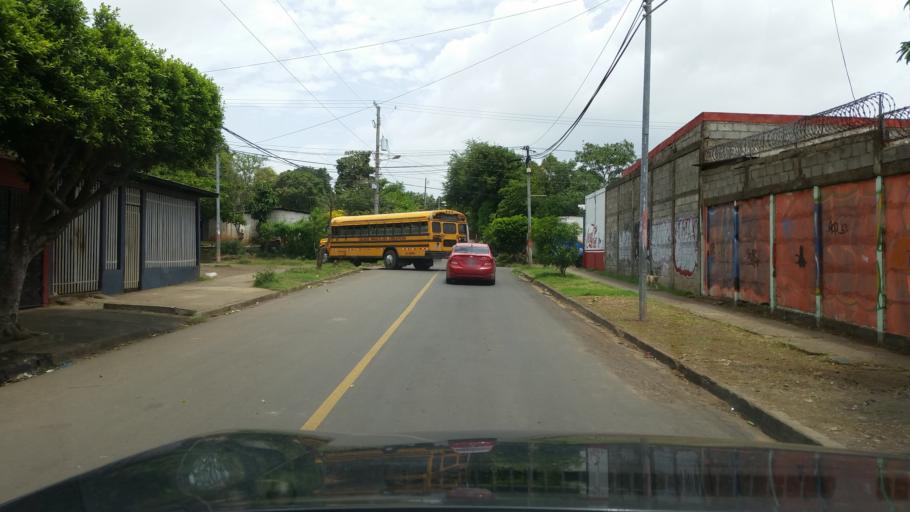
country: NI
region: Managua
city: Managua
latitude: 12.1203
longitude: -86.2213
